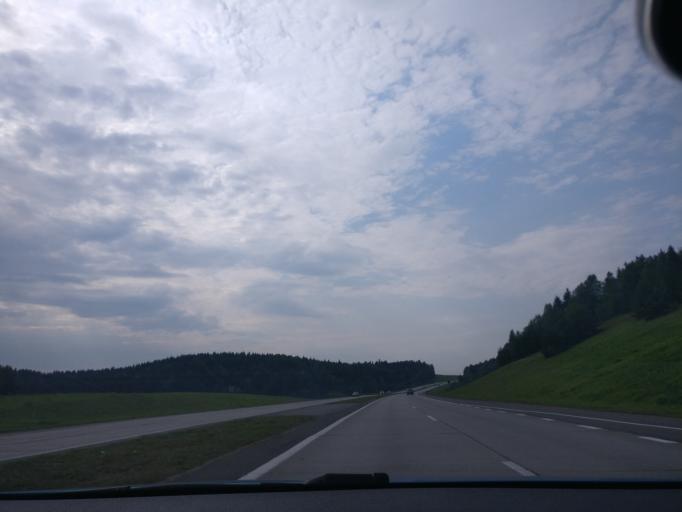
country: BY
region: Minsk
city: Lahoysk
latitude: 54.1110
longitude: 27.8034
